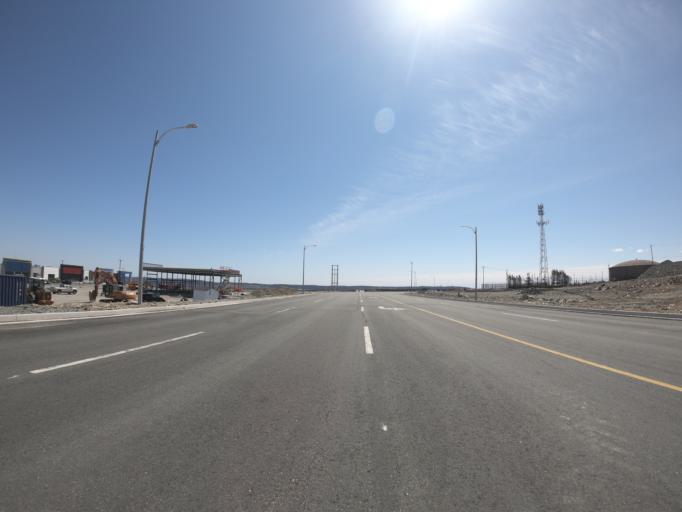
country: CA
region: Newfoundland and Labrador
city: Mount Pearl
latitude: 47.5086
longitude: -52.8315
